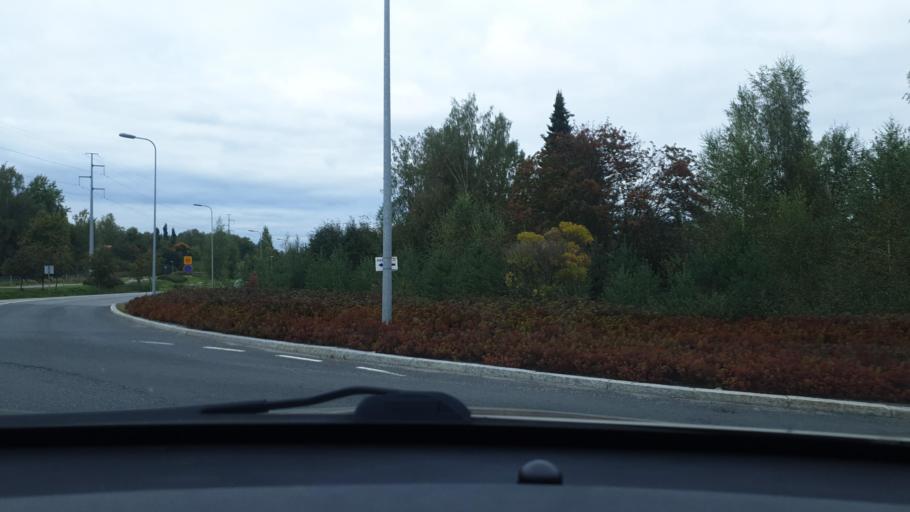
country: FI
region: Ostrobothnia
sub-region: Vaasa
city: Korsholm
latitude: 63.0989
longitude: 21.6614
